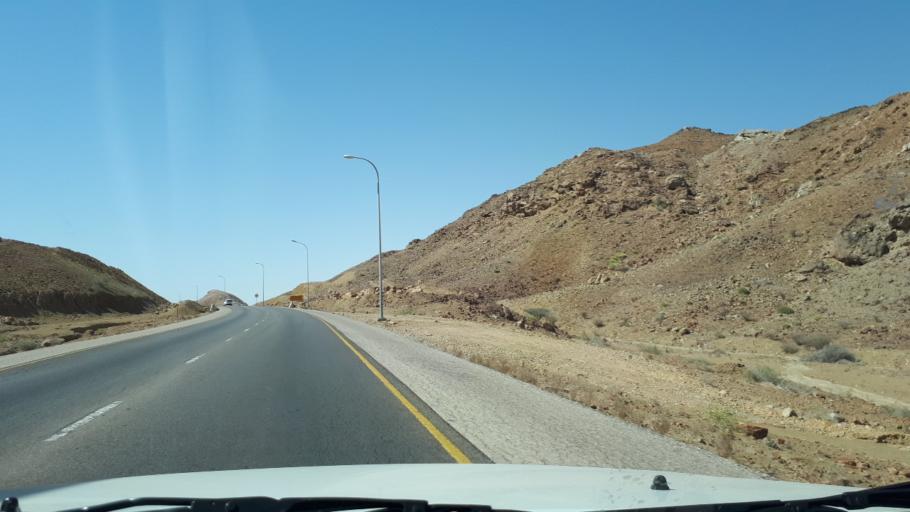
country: OM
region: Ash Sharqiyah
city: Sur
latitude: 22.3242
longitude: 59.3077
